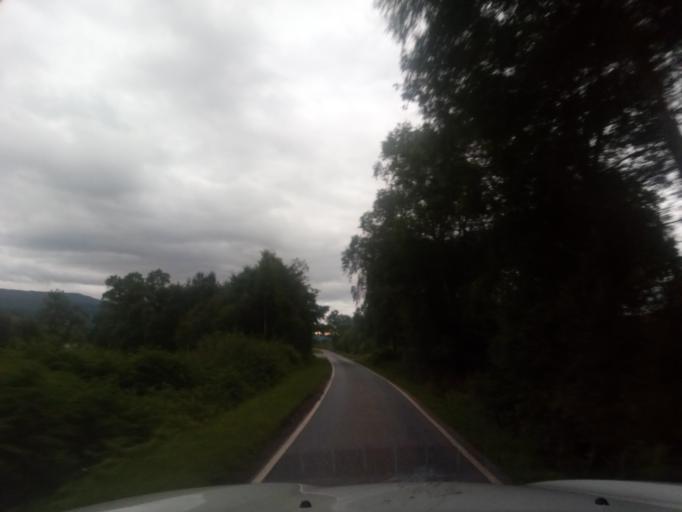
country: GB
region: Scotland
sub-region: Highland
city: Fort William
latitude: 56.8463
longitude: -5.3120
